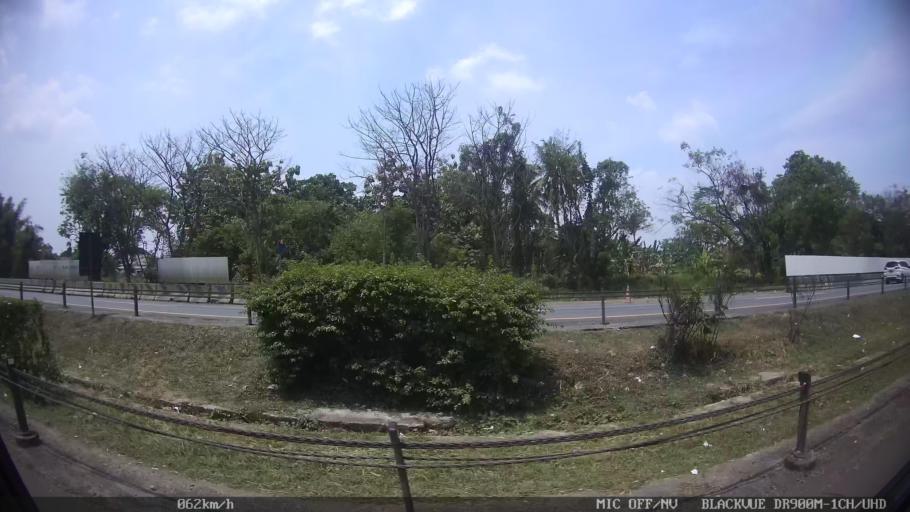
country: ID
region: Banten
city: Serang
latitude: -6.1264
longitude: 106.1921
